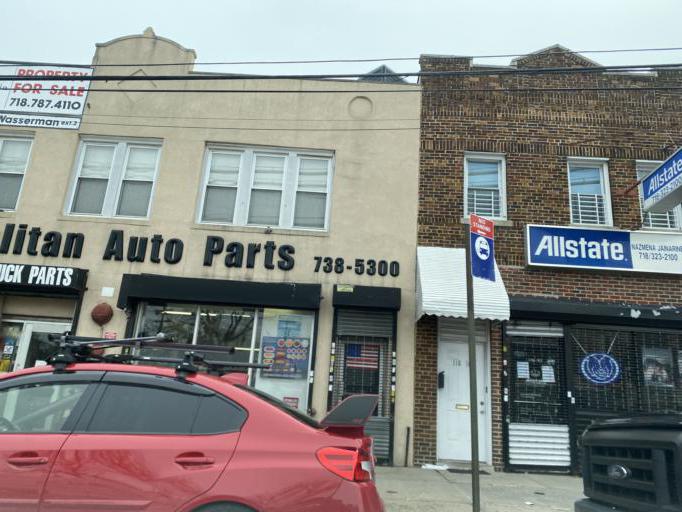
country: US
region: New York
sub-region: Queens County
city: Borough of Queens
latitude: 40.6761
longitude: -73.8196
